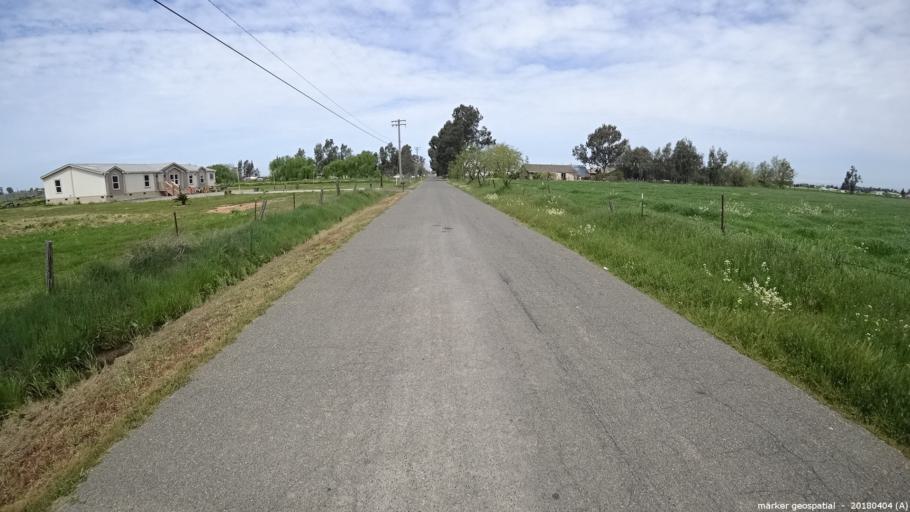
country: US
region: California
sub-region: Sacramento County
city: Herald
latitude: 38.2631
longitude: -121.2358
